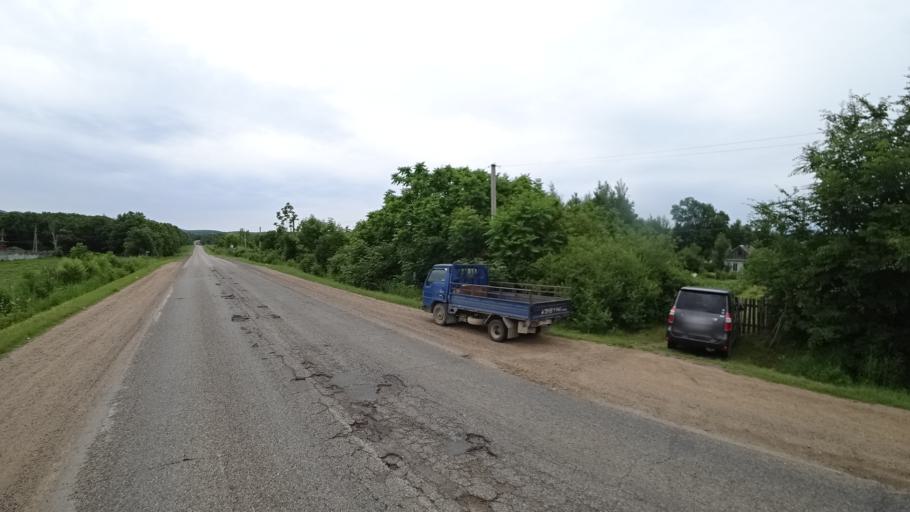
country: RU
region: Primorskiy
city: Novosysoyevka
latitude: 44.1797
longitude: 133.3486
